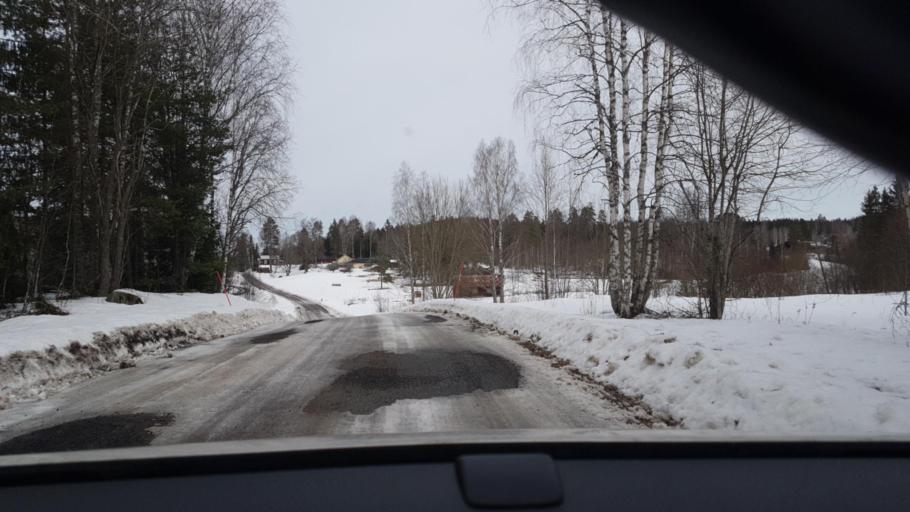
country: SE
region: Vaermland
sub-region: Eda Kommun
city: Amotfors
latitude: 59.8205
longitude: 12.3645
